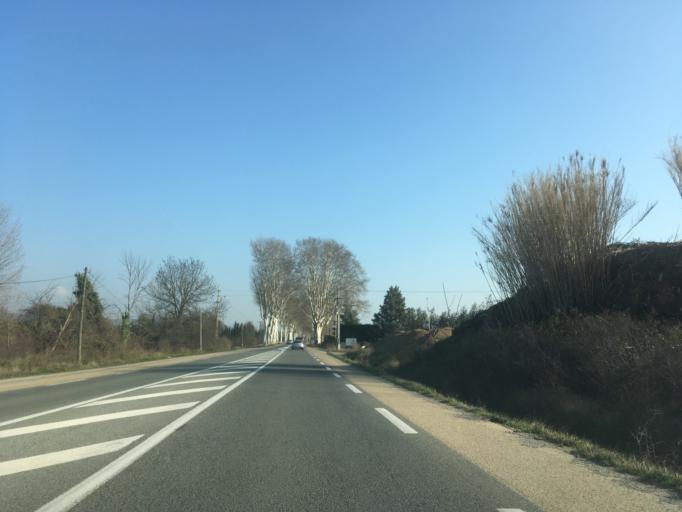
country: FR
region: Provence-Alpes-Cote d'Azur
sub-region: Departement du Var
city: Vidauban
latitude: 43.4392
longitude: 6.4513
